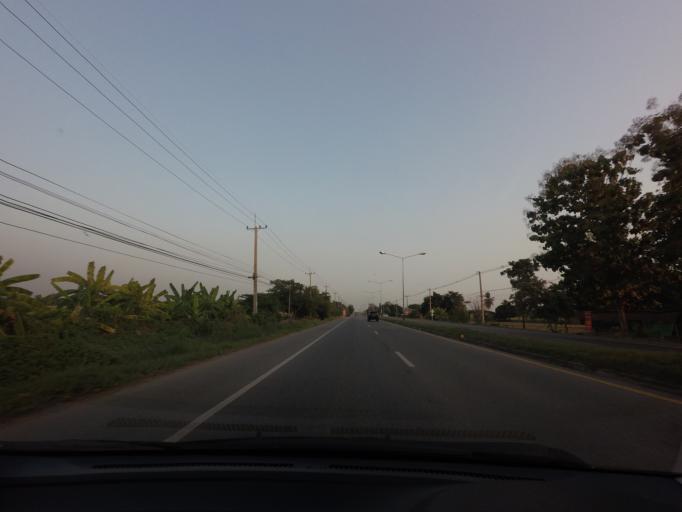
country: TH
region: Sukhothai
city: Kong Krailat
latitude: 17.0123
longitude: 99.9183
